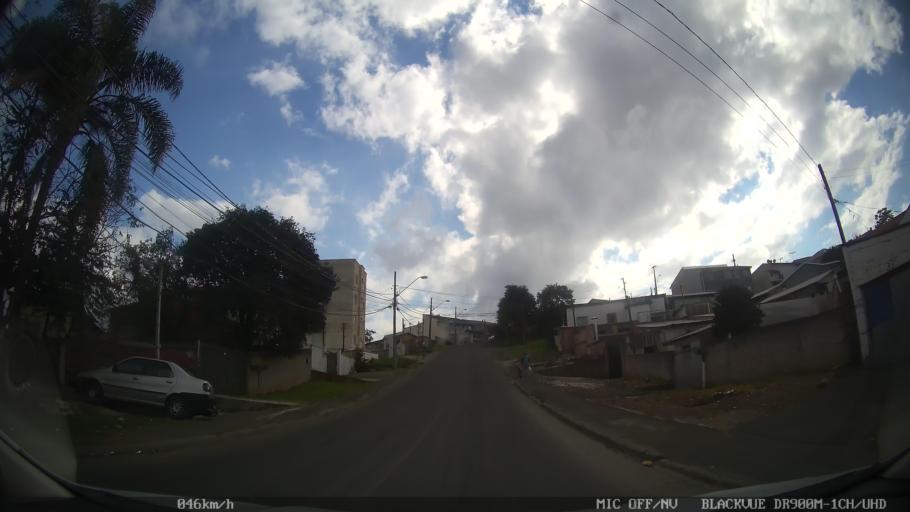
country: BR
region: Parana
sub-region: Colombo
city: Colombo
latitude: -25.3572
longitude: -49.1928
